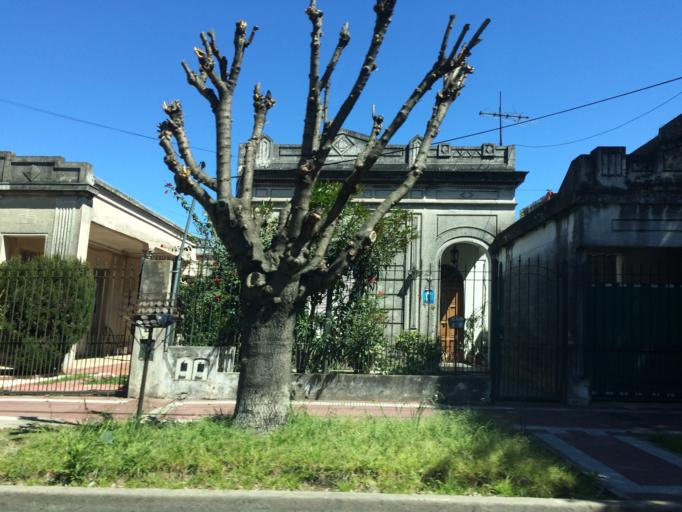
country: AR
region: Buenos Aires
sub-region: Partido de Lanus
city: Lanus
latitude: -34.7234
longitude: -58.3996
